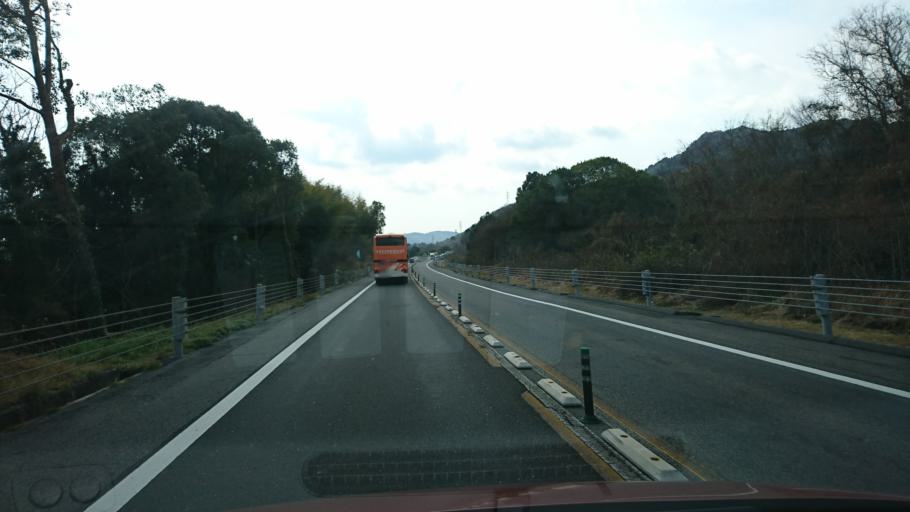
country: JP
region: Hiroshima
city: Innoshima
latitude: 34.2351
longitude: 133.0482
